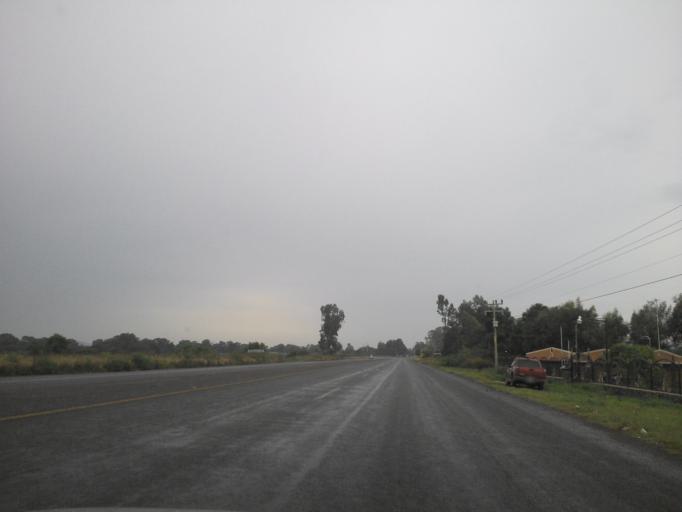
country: MX
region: Jalisco
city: Capilla de Guadalupe
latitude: 20.8518
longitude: -102.6148
